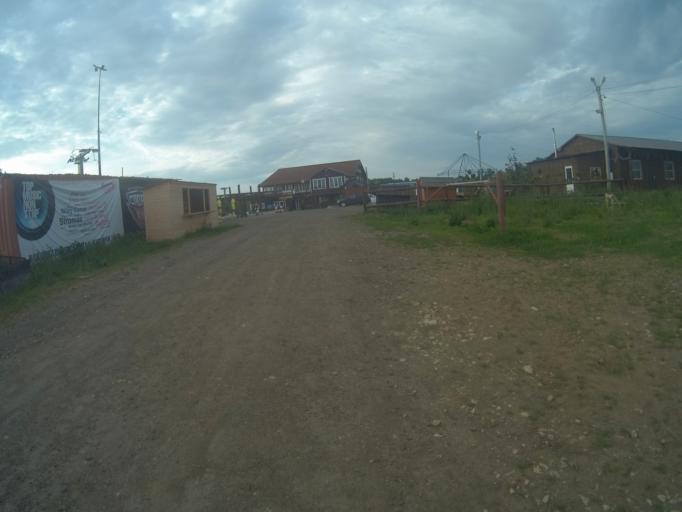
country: RU
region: Vladimir
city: Vladimir
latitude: 56.2137
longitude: 40.3995
